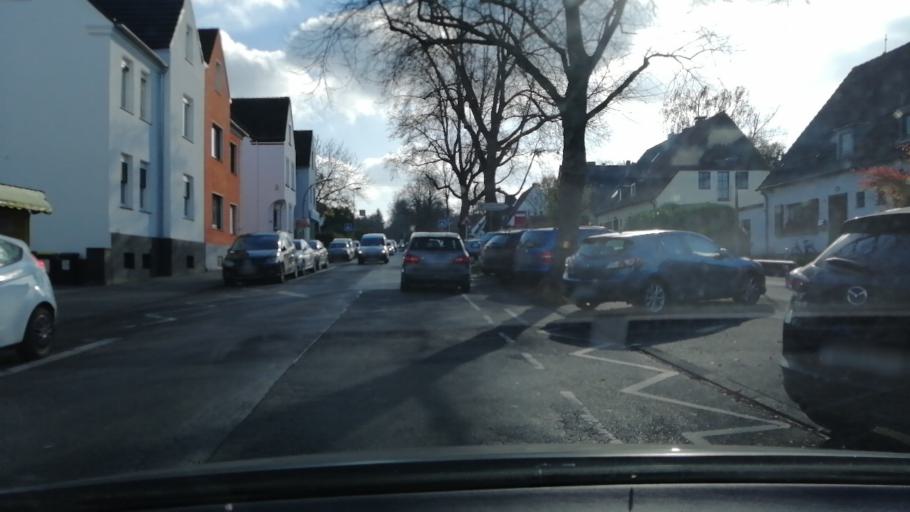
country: DE
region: North Rhine-Westphalia
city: Lanstrop
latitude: 51.5212
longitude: 7.5353
